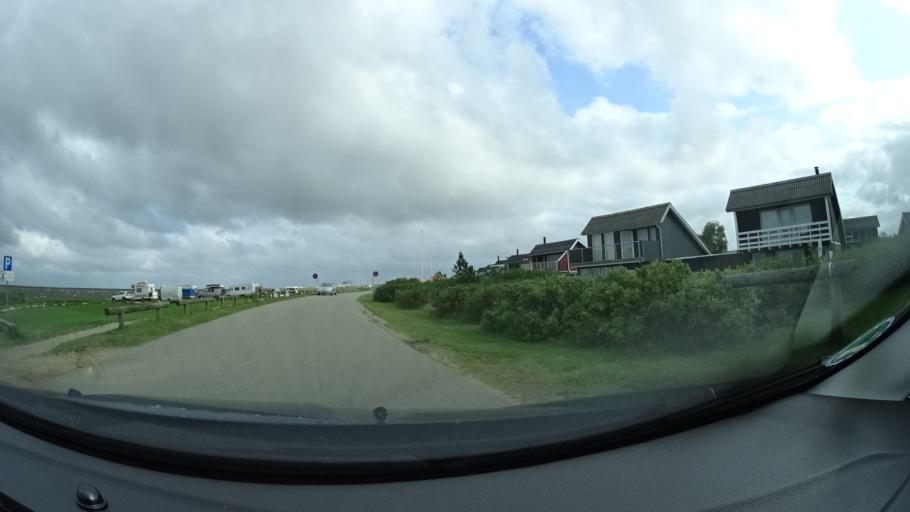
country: DK
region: Central Jutland
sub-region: Ringkobing-Skjern Kommune
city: Hvide Sande
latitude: 55.8444
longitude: 8.2762
